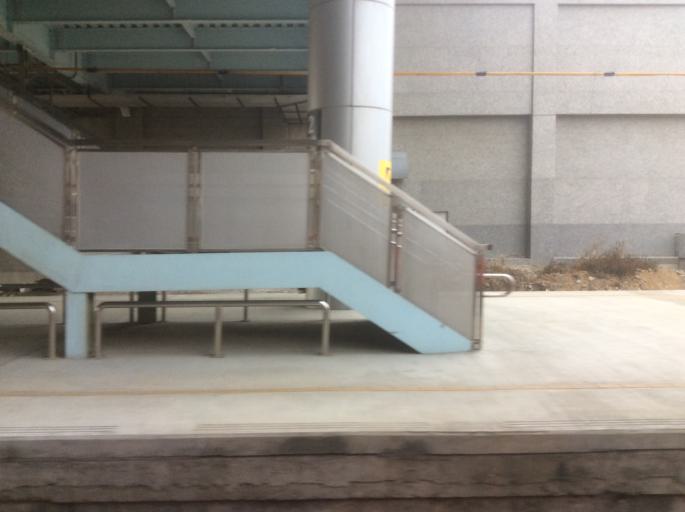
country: TW
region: Taiwan
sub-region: Taichung City
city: Taichung
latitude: 24.2371
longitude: 120.5572
